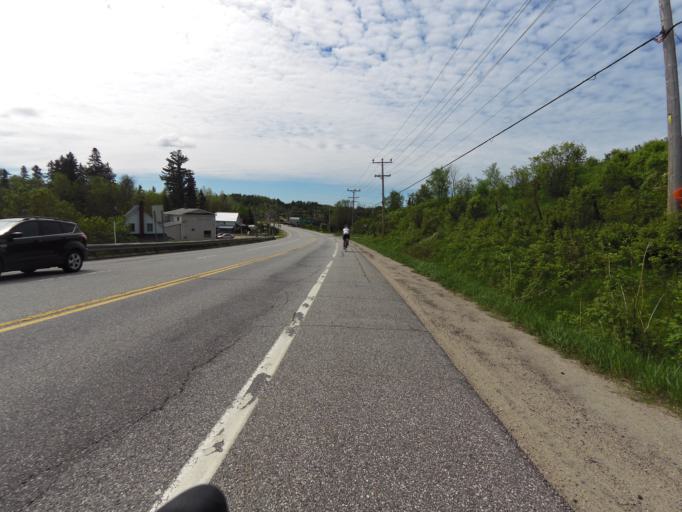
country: CA
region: Quebec
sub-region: Outaouais
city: Wakefield
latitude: 45.8140
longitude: -75.9531
